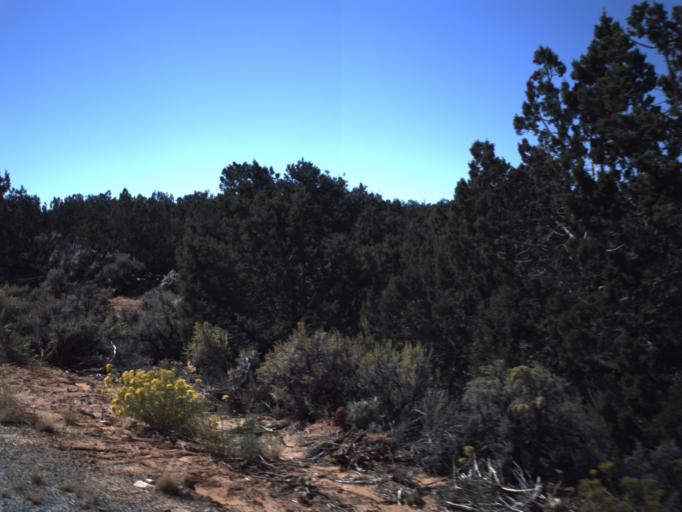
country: US
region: Utah
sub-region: San Juan County
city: Blanding
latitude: 37.4681
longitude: -109.9111
